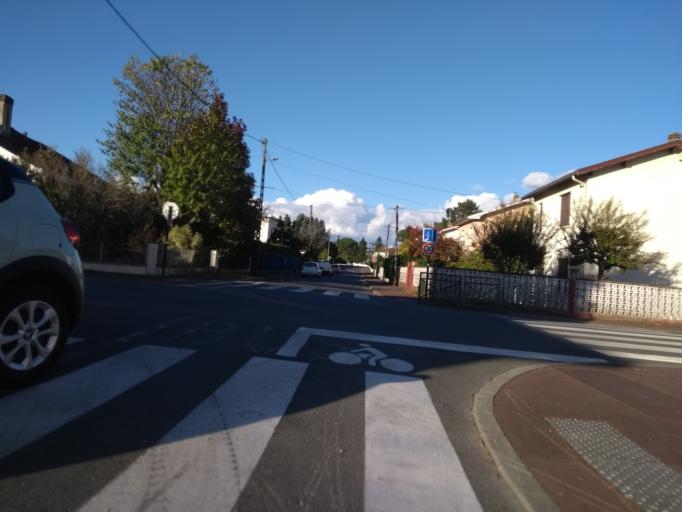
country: FR
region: Aquitaine
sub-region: Departement de la Gironde
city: Gradignan
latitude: 44.7733
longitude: -0.6113
